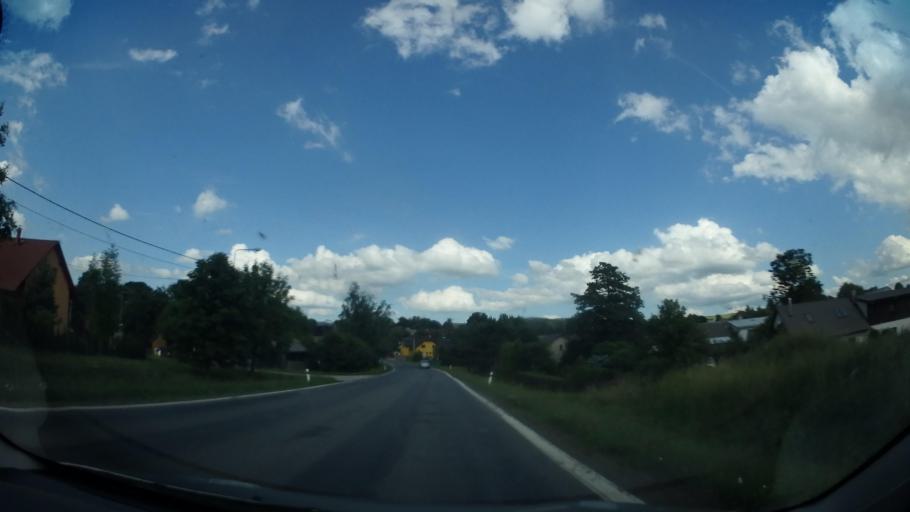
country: CZ
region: Vysocina
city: Zd'ar nad Sazavou Druhy
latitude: 49.6187
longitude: 15.9507
